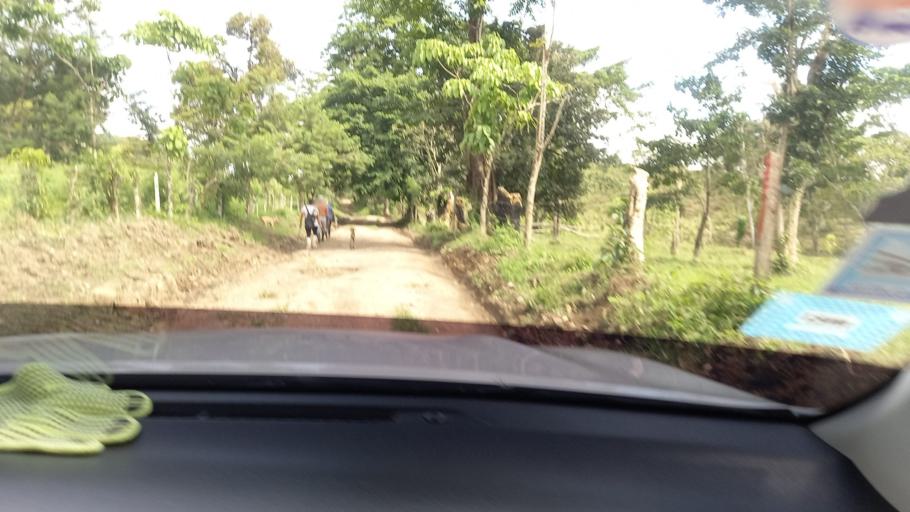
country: NI
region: Jinotega
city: San Jose de Bocay
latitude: 13.3930
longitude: -85.6938
